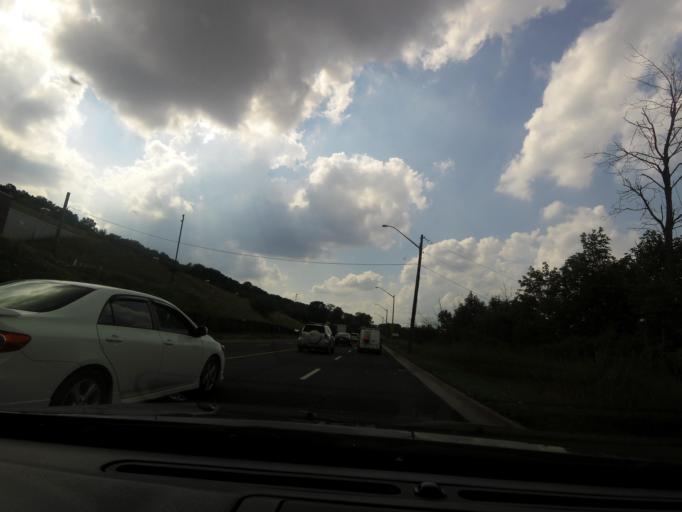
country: CA
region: Ontario
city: Hamilton
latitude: 43.2321
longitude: -79.8185
